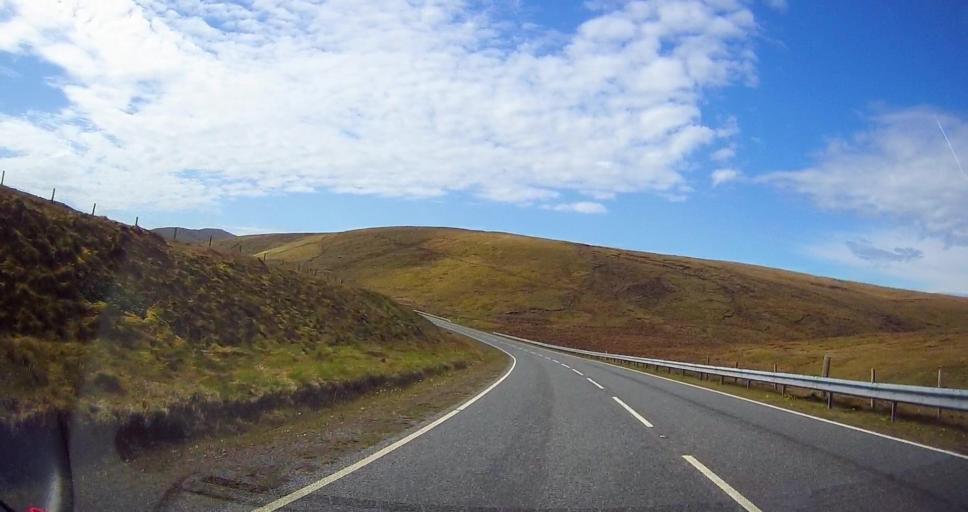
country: GB
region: Scotland
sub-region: Shetland Islands
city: Sandwick
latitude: 60.0059
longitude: -1.2767
